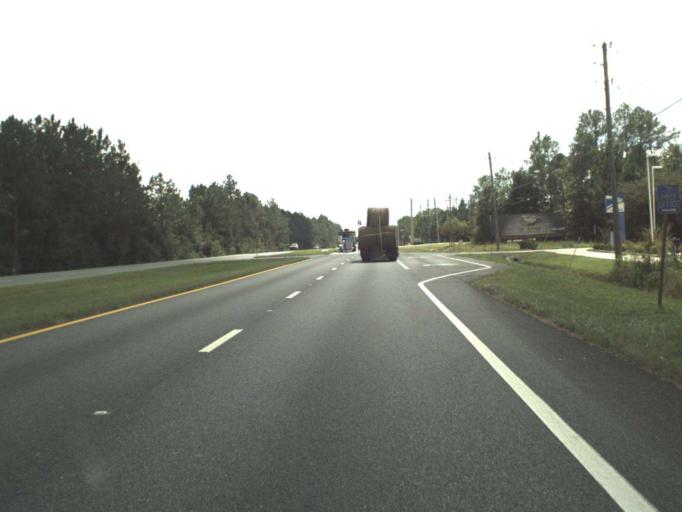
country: US
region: Florida
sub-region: Bay County
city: Youngstown
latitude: 30.3623
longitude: -85.4384
